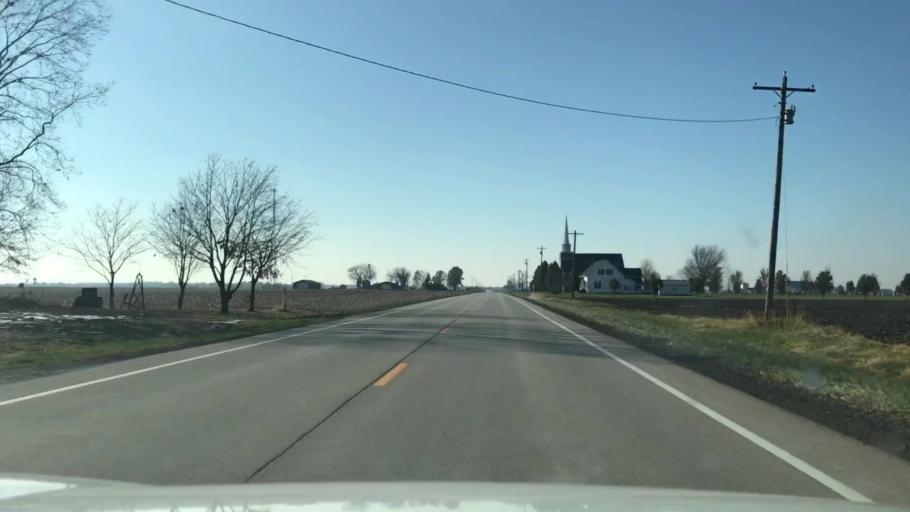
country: US
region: Illinois
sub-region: Washington County
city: Okawville
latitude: 38.4422
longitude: -89.4887
